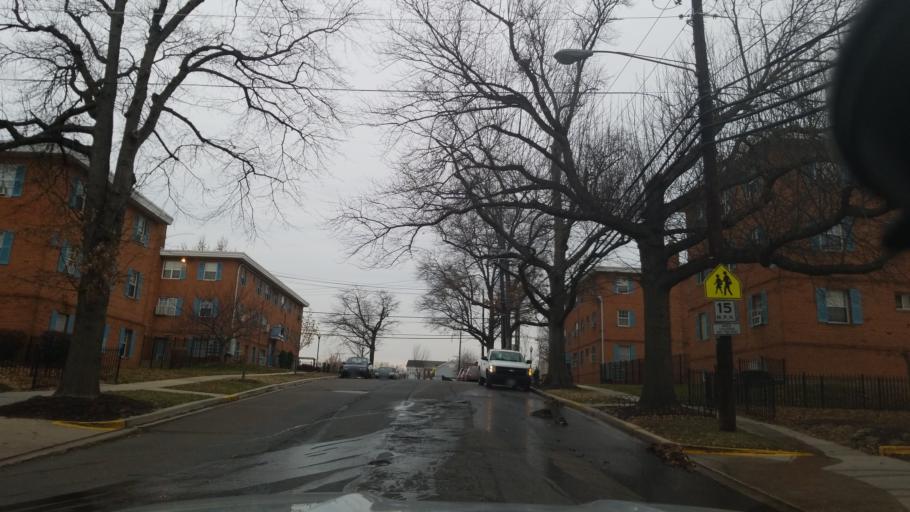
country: US
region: Maryland
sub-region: Prince George's County
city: Hillcrest Heights
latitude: 38.8466
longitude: -76.9787
